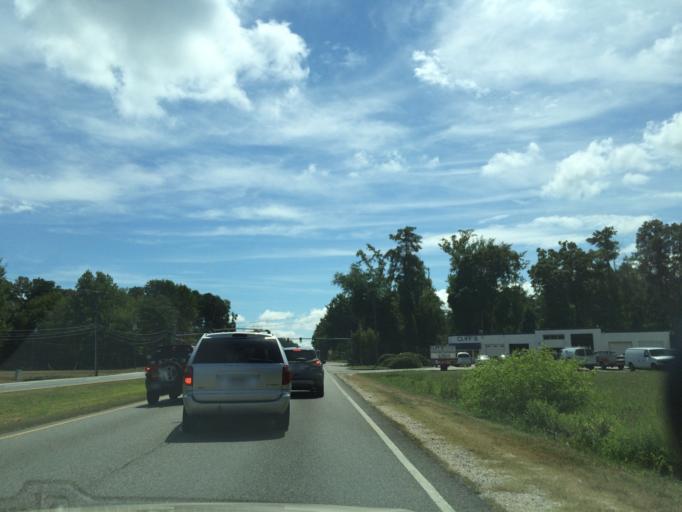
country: US
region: Virginia
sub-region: York County
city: Yorktown
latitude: 37.1956
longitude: -76.4911
